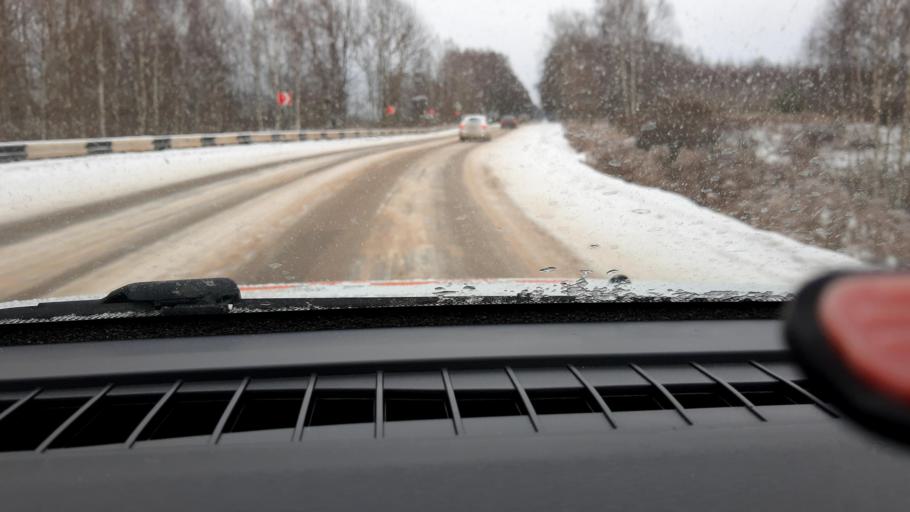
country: RU
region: Nizjnij Novgorod
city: Afonino
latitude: 56.3119
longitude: 44.2288
